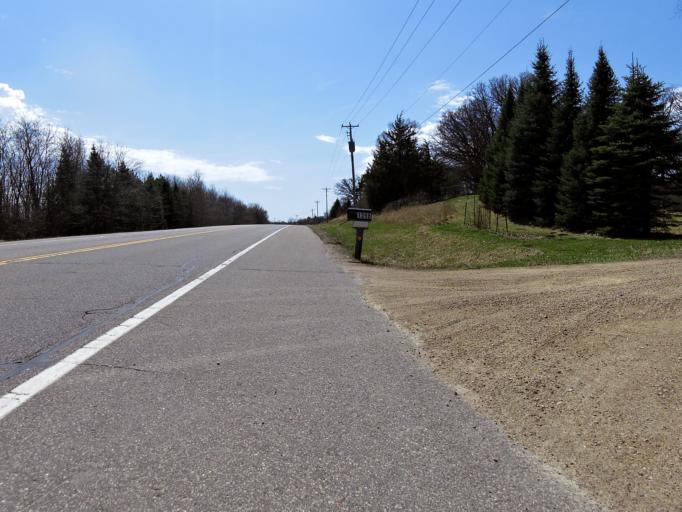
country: US
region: Minnesota
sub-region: Washington County
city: Lakeland
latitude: 44.9692
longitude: -92.7950
